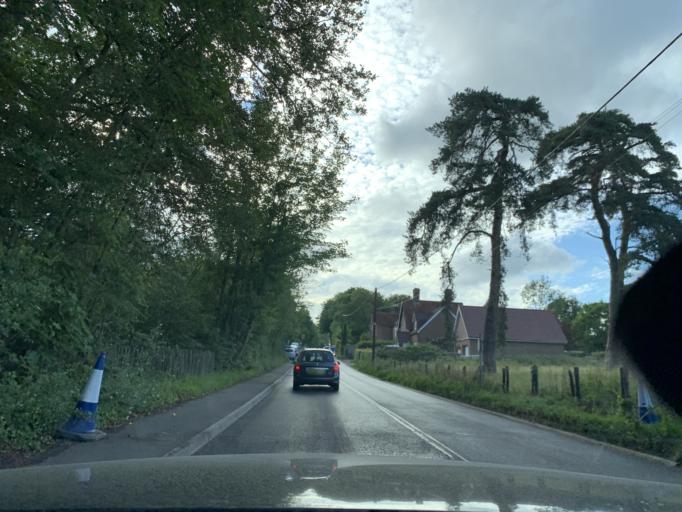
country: GB
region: England
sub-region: East Sussex
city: Robertsbridge
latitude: 50.9563
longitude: 0.4979
